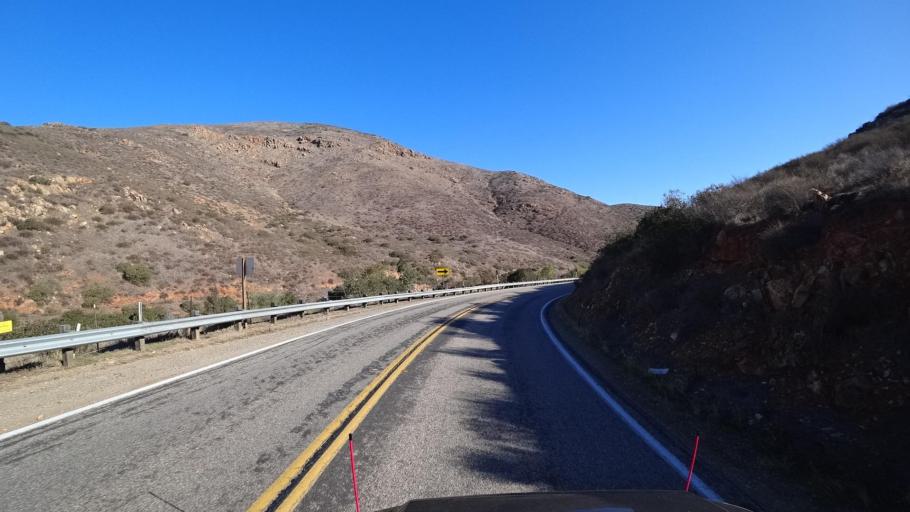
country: US
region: California
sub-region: San Diego County
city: Jamul
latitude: 32.6385
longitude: -116.8833
